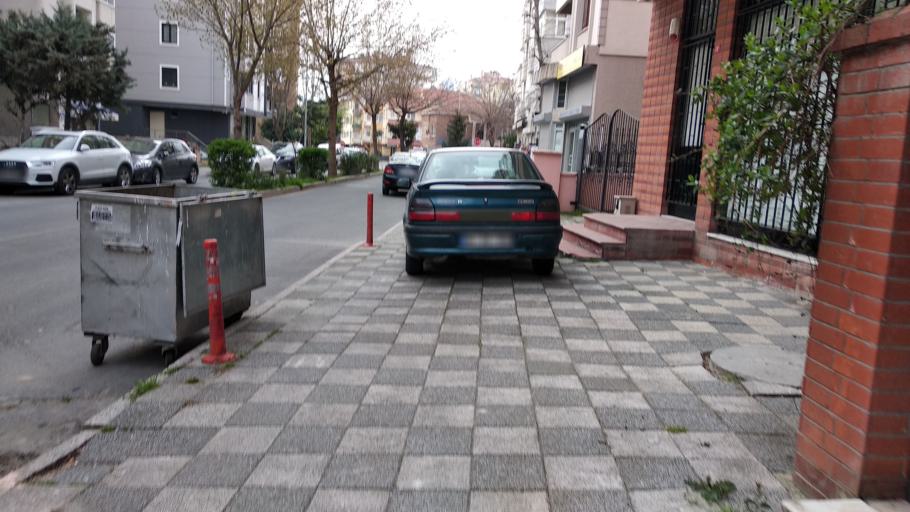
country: TR
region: Istanbul
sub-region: Atasehir
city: Atasehir
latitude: 40.9716
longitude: 29.1147
